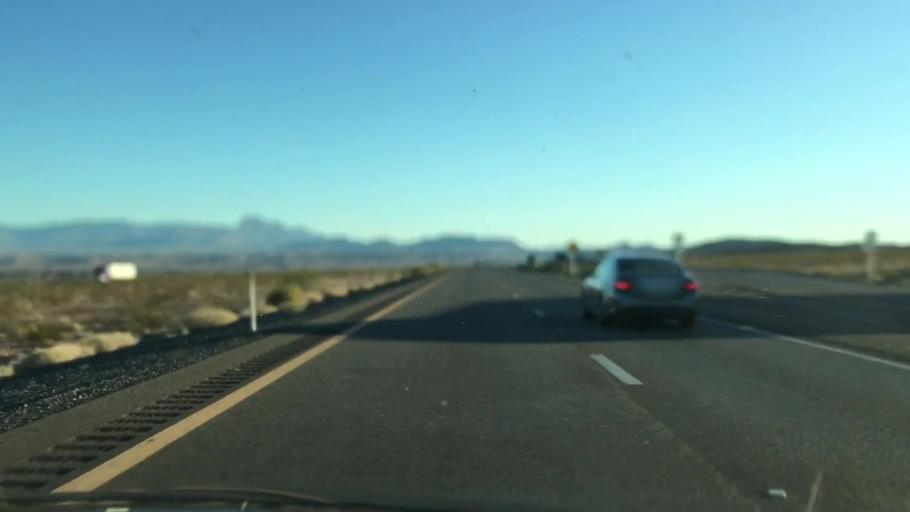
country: US
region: Nevada
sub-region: Clark County
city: Moapa Town
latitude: 36.6266
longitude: -114.6105
